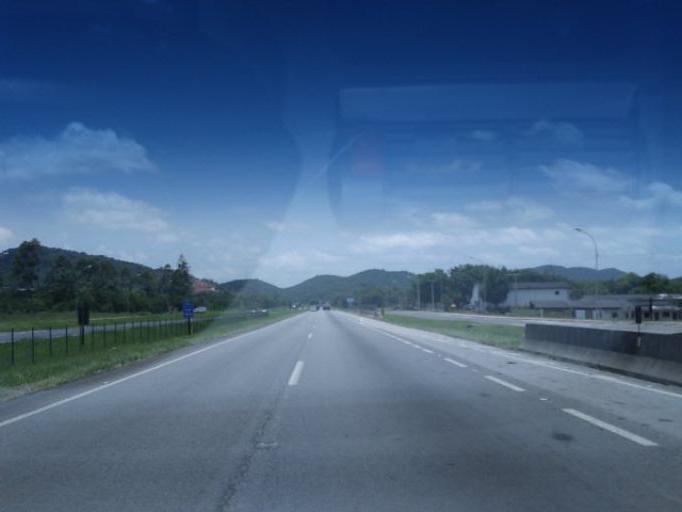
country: BR
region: Sao Paulo
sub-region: Juquia
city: Juquia
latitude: -24.3392
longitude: -47.6447
